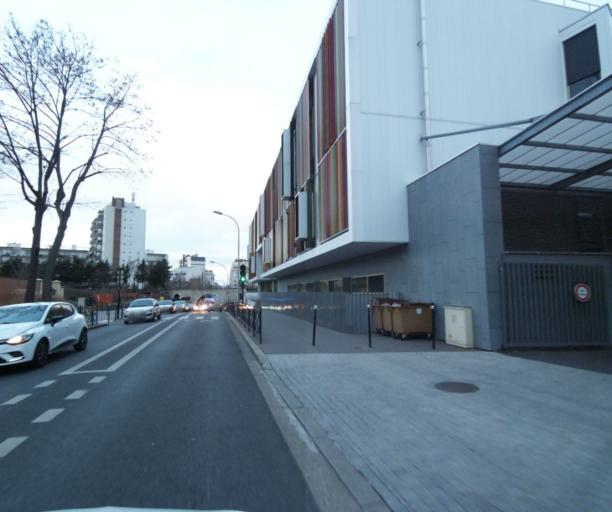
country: FR
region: Ile-de-France
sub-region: Departement des Hauts-de-Seine
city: Courbevoie
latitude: 48.9001
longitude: 2.2565
